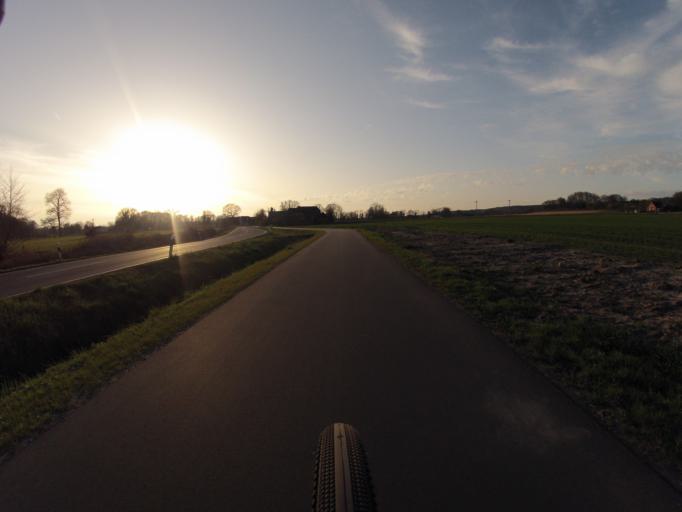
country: DE
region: North Rhine-Westphalia
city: Ibbenburen
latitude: 52.2328
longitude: 7.7043
